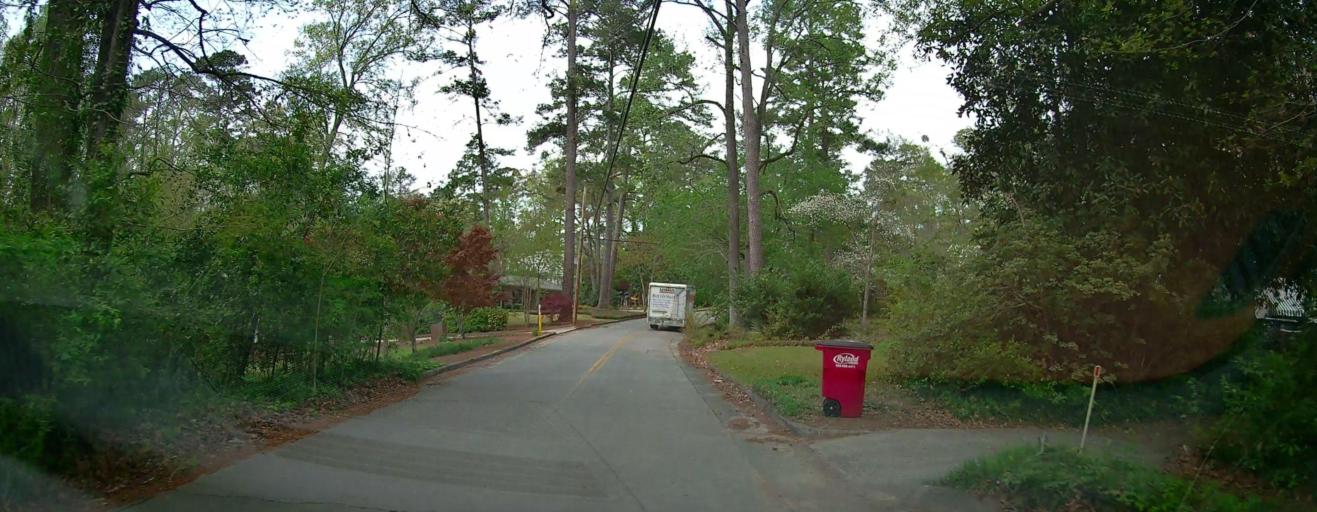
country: US
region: Georgia
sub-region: Bibb County
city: Macon
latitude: 32.8545
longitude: -83.6698
